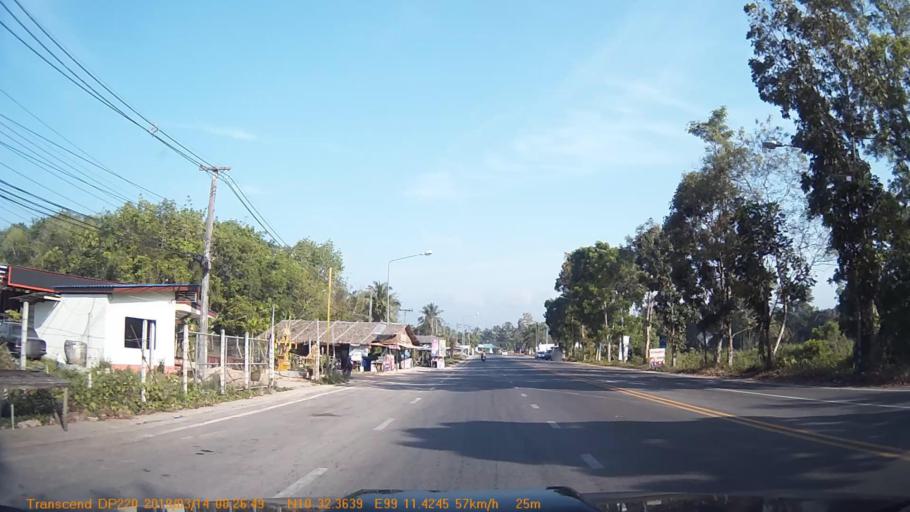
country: TH
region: Chumphon
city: Chumphon
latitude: 10.5396
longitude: 99.1903
